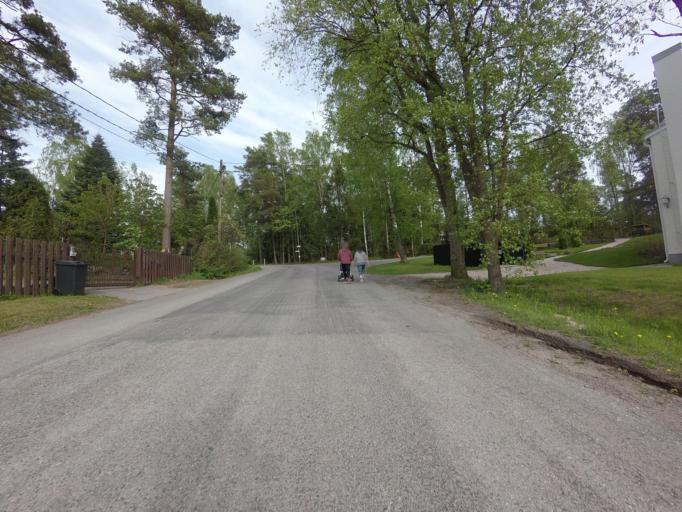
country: FI
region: Uusimaa
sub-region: Helsinki
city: Espoo
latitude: 60.1435
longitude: 24.6877
